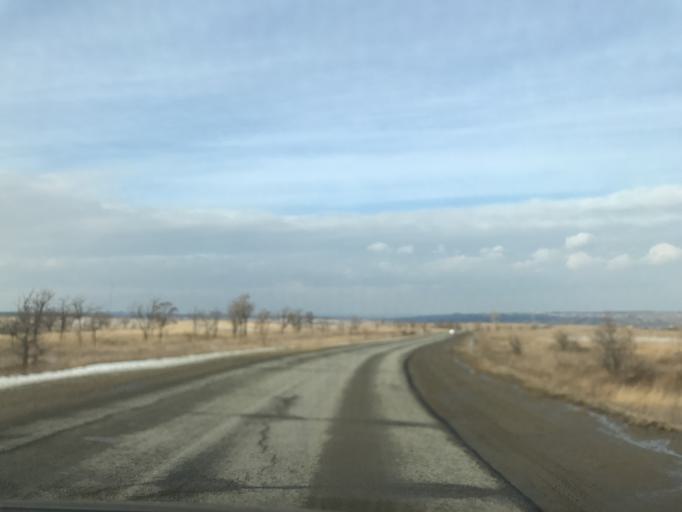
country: RU
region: Rostov
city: Staraya Stanitsa
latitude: 48.2715
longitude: 40.3490
